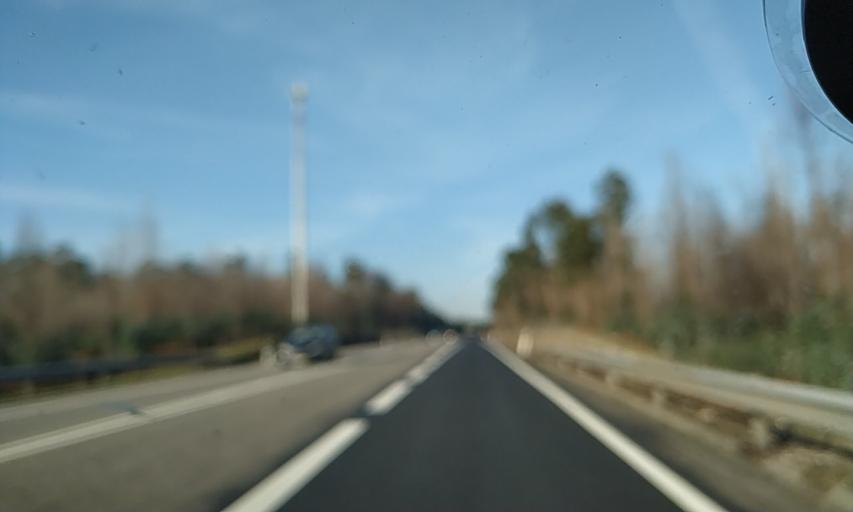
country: PT
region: Viseu
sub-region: Concelho de Tondela
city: Tondela
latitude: 40.5594
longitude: -8.0513
